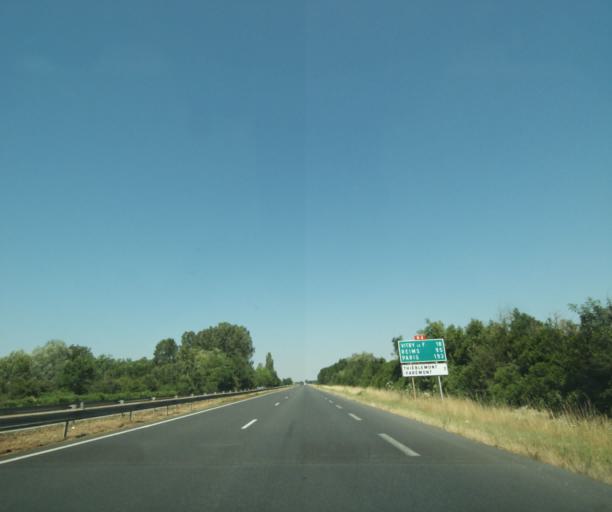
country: FR
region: Champagne-Ardenne
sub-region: Departement de la Haute-Marne
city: Villiers-en-Lieu
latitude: 48.6603
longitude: 4.8077
